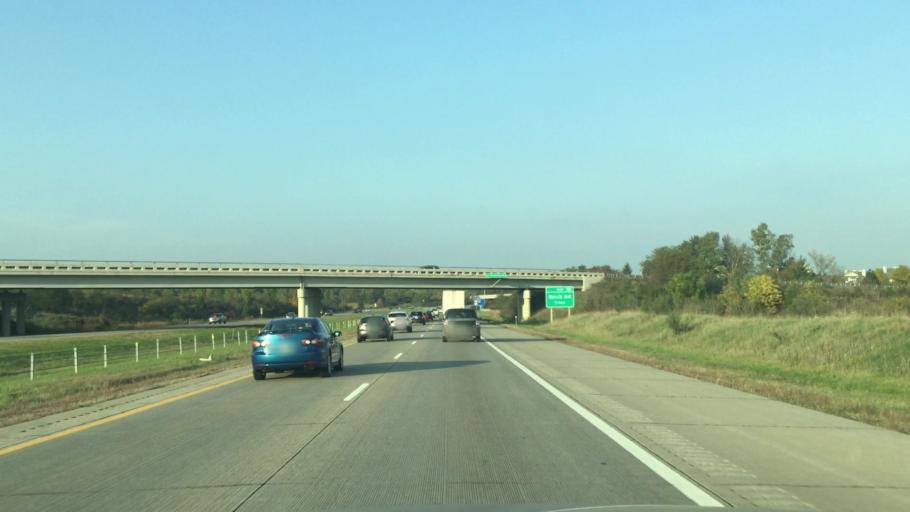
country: US
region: Michigan
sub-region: Wayne County
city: Plymouth
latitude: 42.3745
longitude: -83.5352
